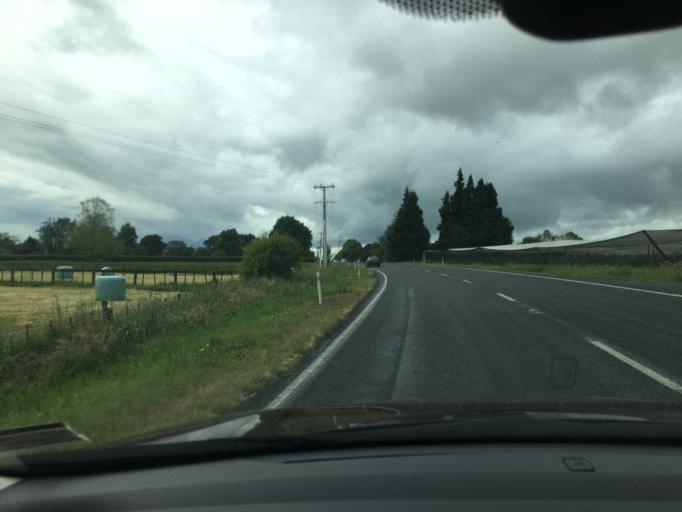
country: NZ
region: Waikato
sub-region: Waipa District
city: Cambridge
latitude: -37.9140
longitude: 175.4493
